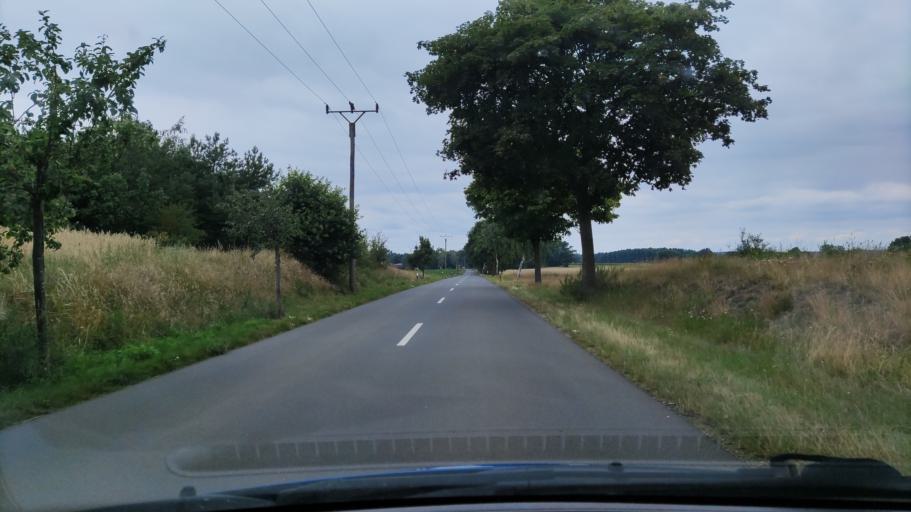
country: DE
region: Lower Saxony
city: Rosche
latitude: 53.0056
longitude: 10.7588
